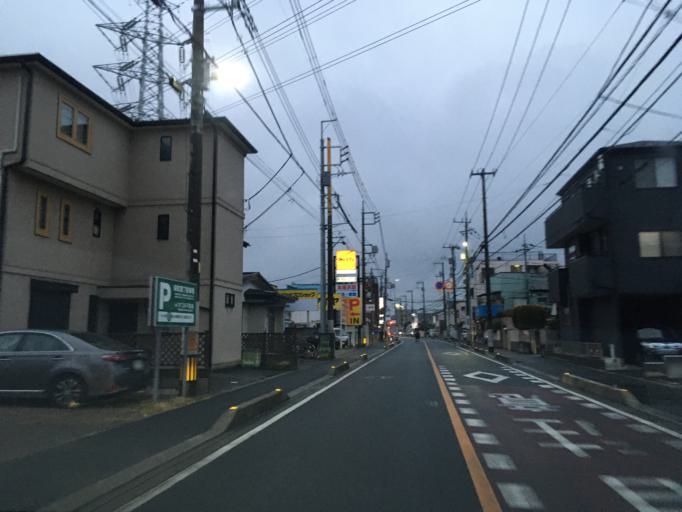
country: JP
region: Saitama
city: Asaka
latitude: 35.7887
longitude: 139.5942
